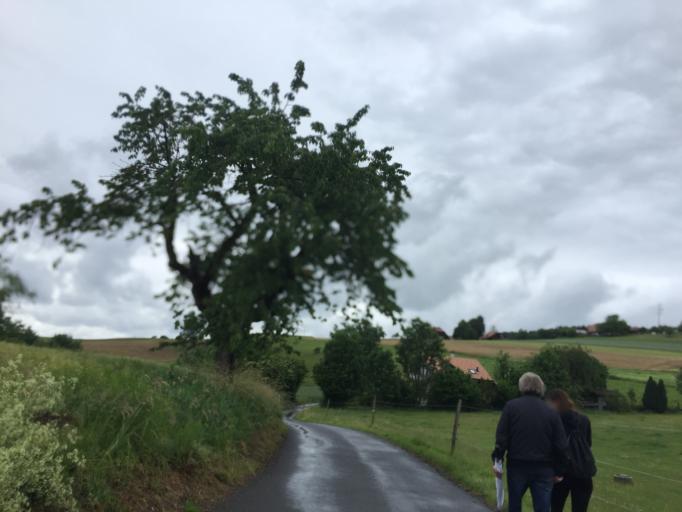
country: CH
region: Bern
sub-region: Bern-Mittelland District
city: Taegertschi
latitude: 46.8855
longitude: 7.5818
